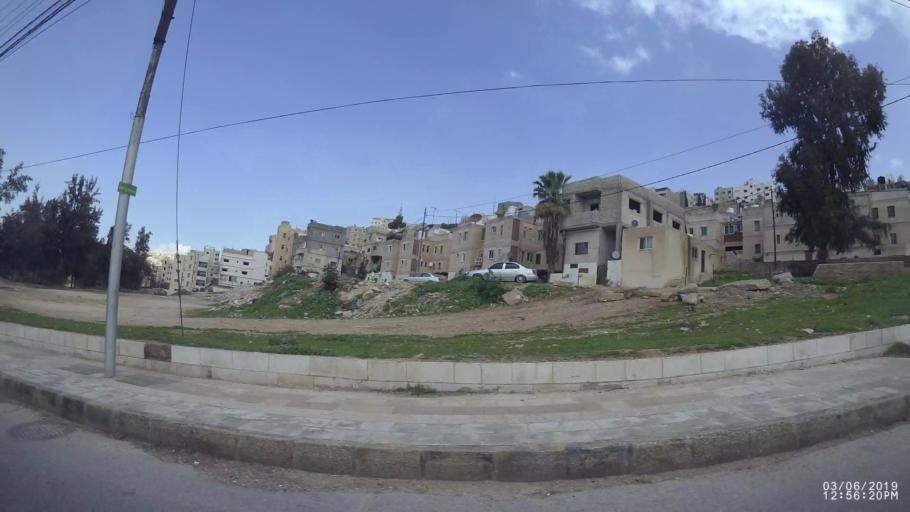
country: JO
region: Amman
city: Amman
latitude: 31.9803
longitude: 35.9777
